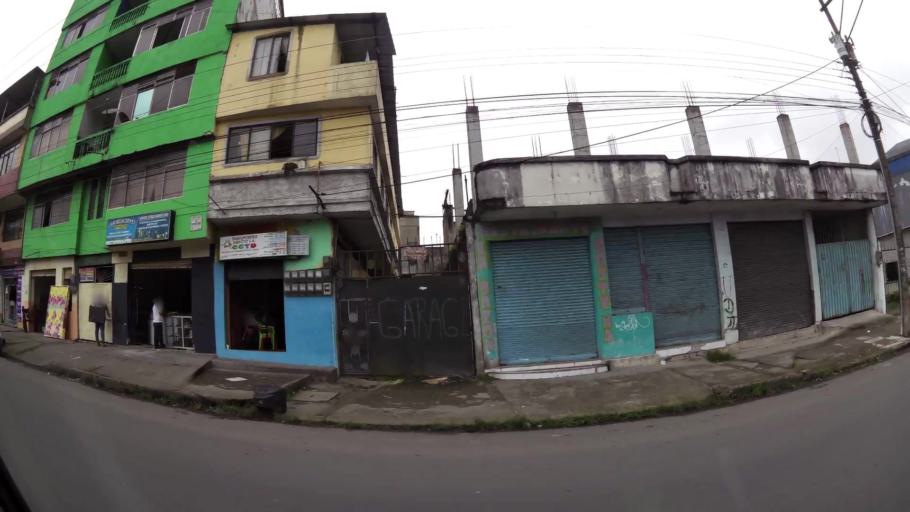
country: EC
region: Santo Domingo de los Tsachilas
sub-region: Canton Santo Domingo de los Colorados
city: Santo Domingo de los Colorados
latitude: -0.2464
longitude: -79.1739
